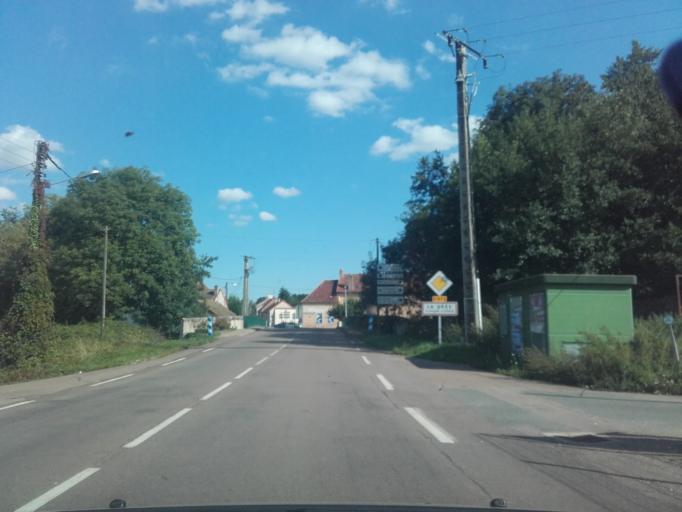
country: FR
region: Bourgogne
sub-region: Departement de Saone-et-Loire
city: Epinac
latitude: 46.9741
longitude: 4.4971
